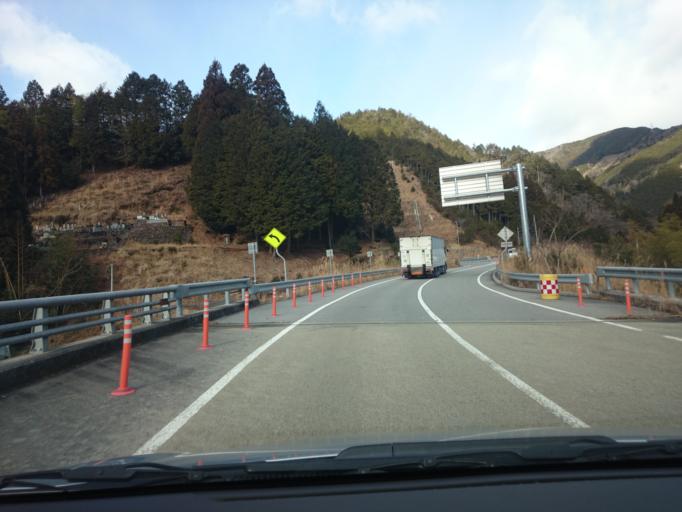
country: JP
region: Gifu
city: Gujo
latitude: 35.7480
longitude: 137.2079
